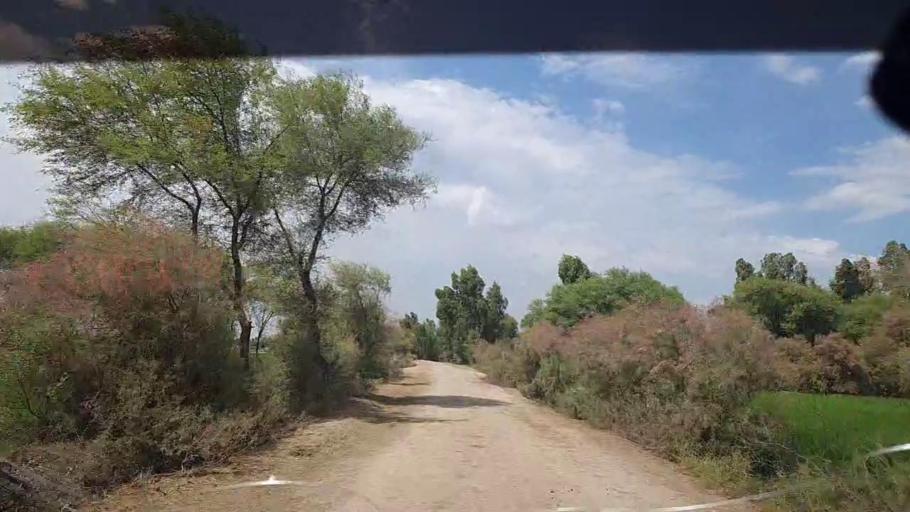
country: PK
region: Sindh
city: Ghauspur
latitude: 28.1503
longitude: 68.9974
